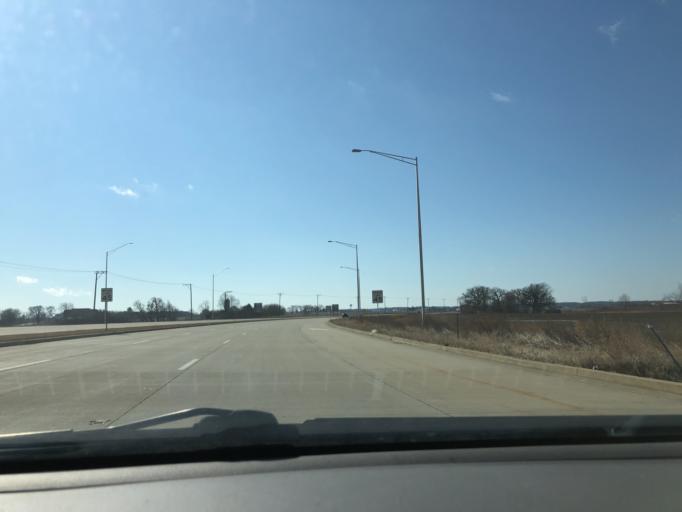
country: US
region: Illinois
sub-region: McHenry County
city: Huntley
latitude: 42.1197
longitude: -88.4331
